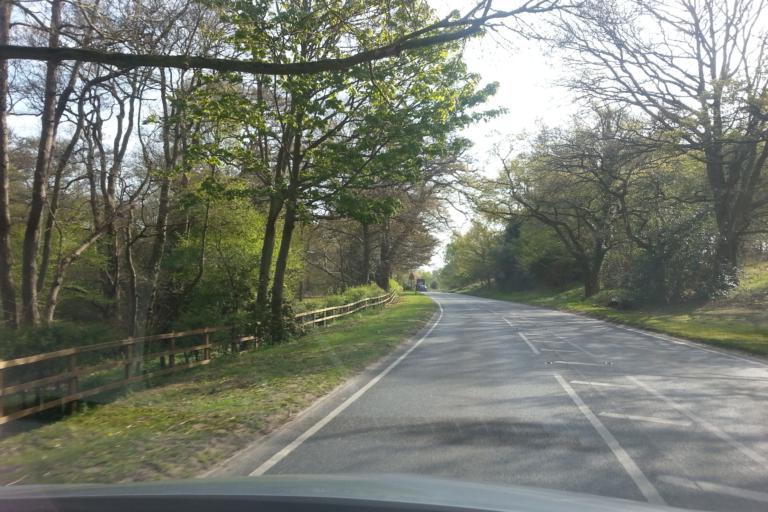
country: GB
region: England
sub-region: Suffolk
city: Woodbridge
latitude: 52.1017
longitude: 1.3512
